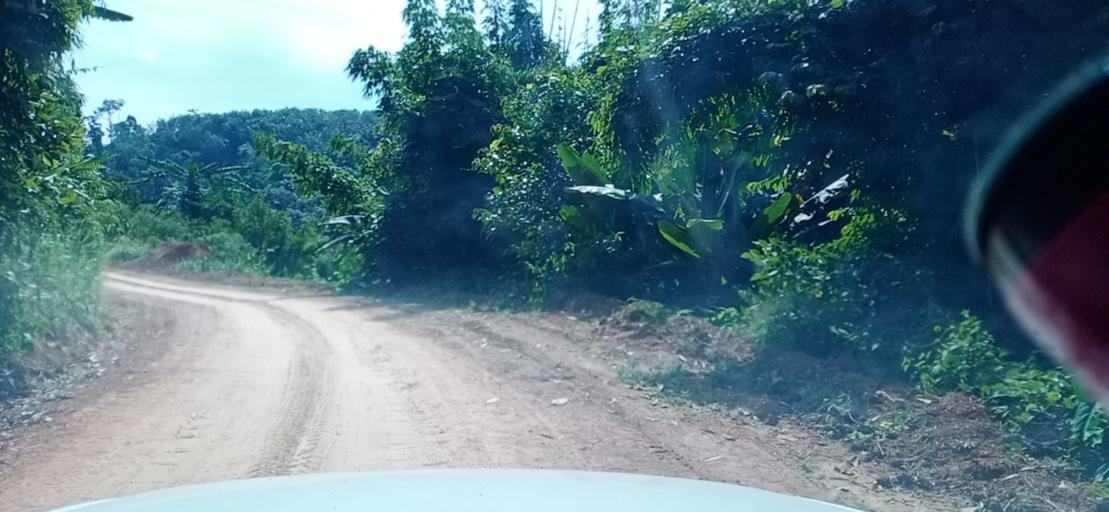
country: TH
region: Changwat Bueng Kan
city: Pak Khat
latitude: 18.6379
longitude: 103.2541
